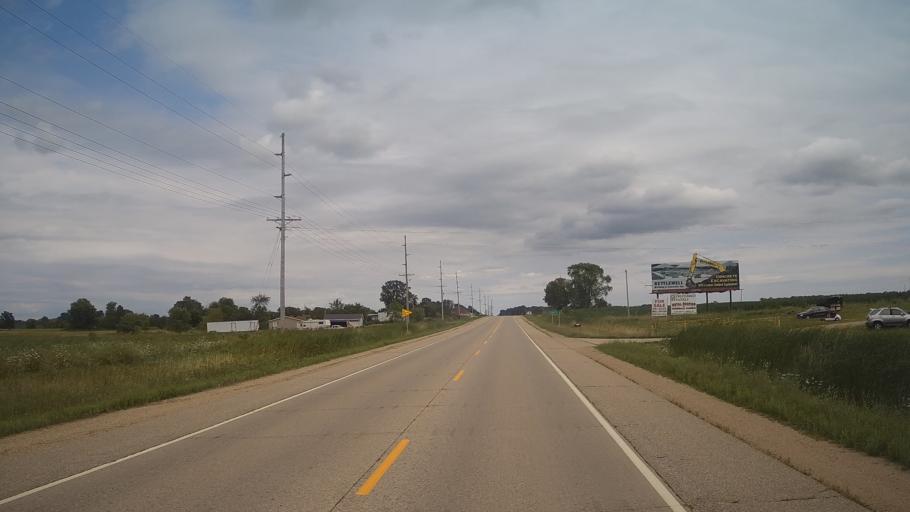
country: US
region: Wisconsin
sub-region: Waushara County
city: Redgranite
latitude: 44.0413
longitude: -89.0205
